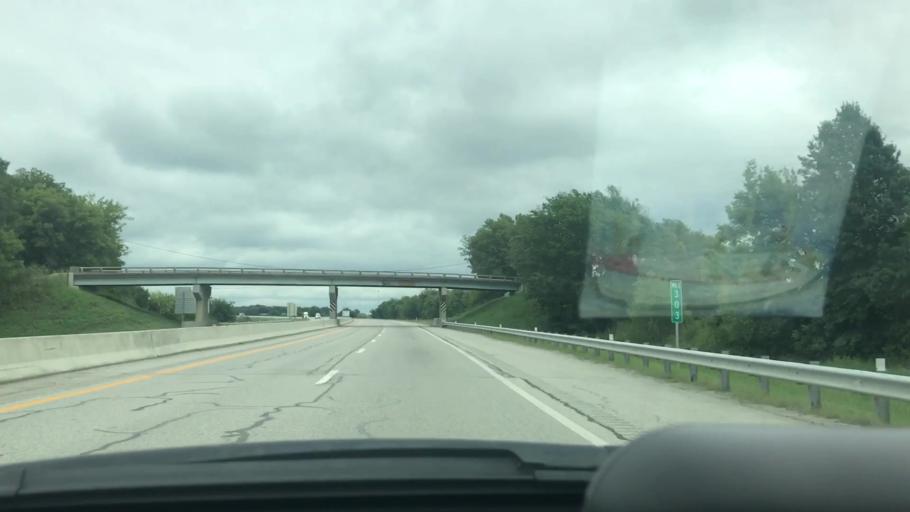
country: US
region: Oklahoma
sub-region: Ottawa County
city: Afton
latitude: 36.7280
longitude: -94.9209
